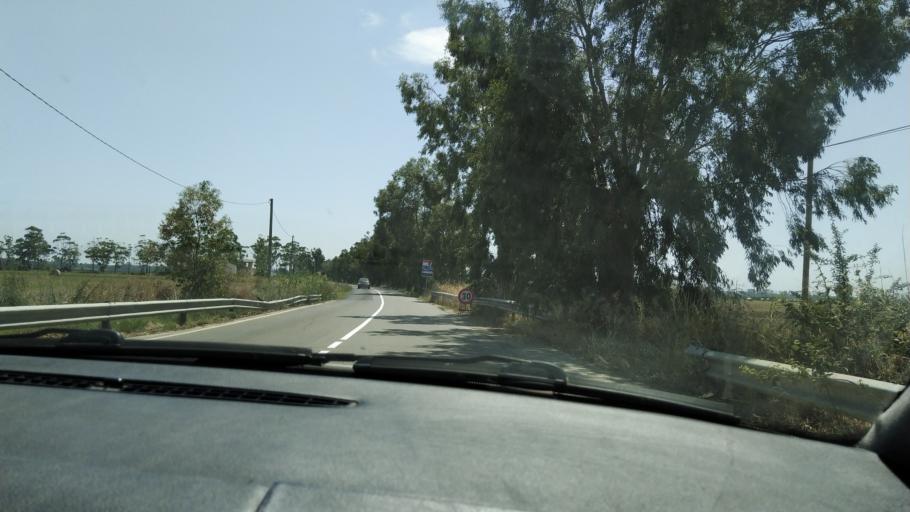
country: IT
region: Basilicate
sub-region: Provincia di Matera
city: Marconia
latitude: 40.3342
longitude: 16.7762
